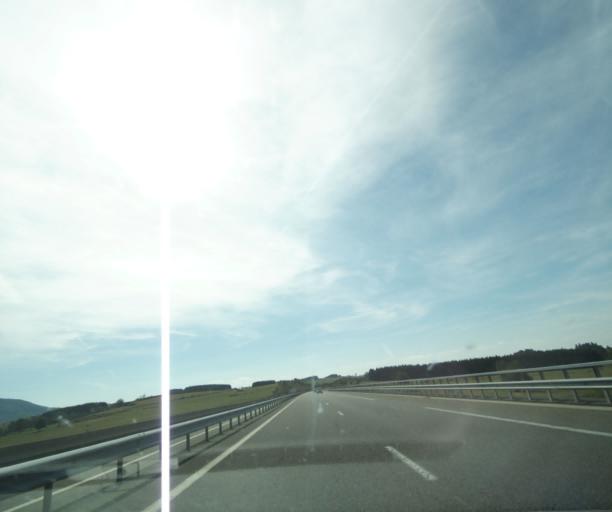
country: FR
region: Auvergne
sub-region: Departement du Puy-de-Dome
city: Saint-Ours
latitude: 45.8937
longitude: 2.9343
